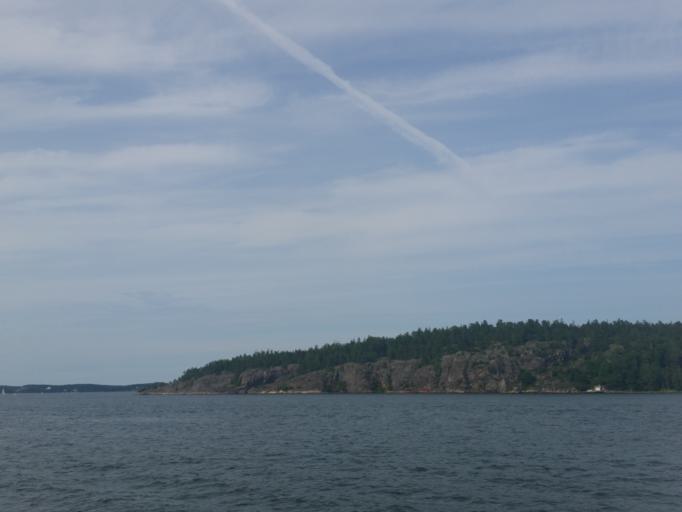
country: SE
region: Stockholm
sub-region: Nacka Kommun
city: Saltsjobaden
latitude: 59.2772
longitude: 18.3282
